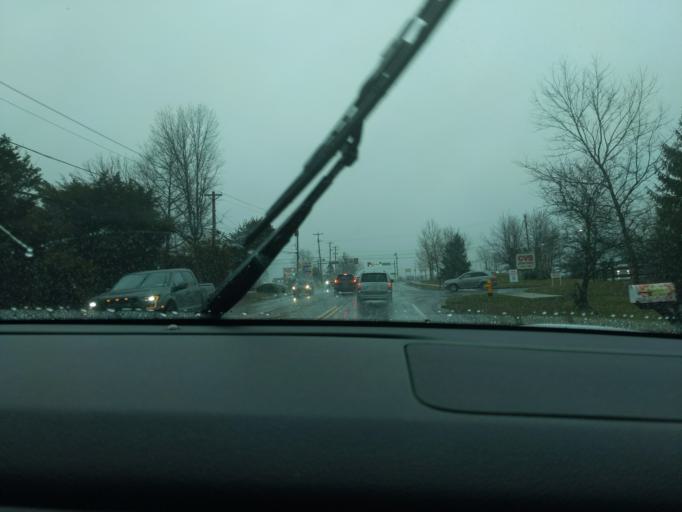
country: US
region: Pennsylvania
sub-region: Bucks County
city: Dublin
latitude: 40.3831
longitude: -75.2210
